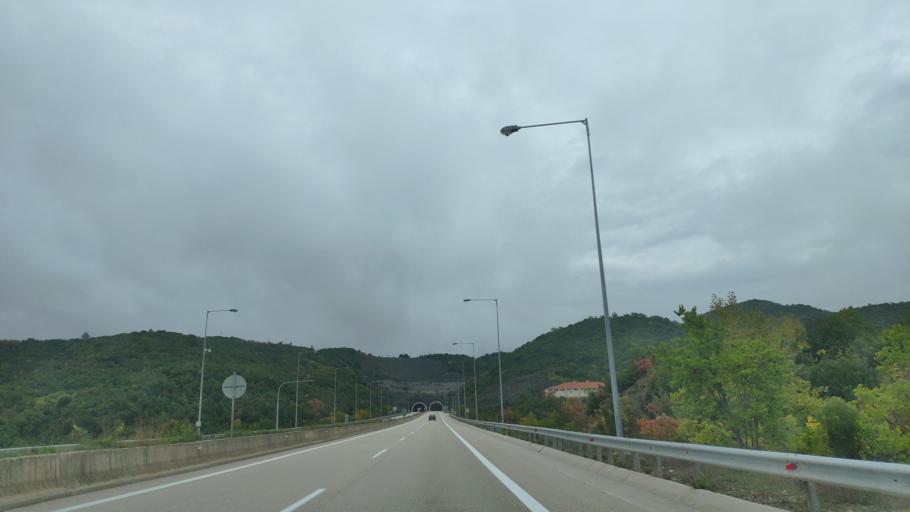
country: GR
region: Epirus
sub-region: Nomos Ioanninon
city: Pedini
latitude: 39.5439
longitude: 20.7100
